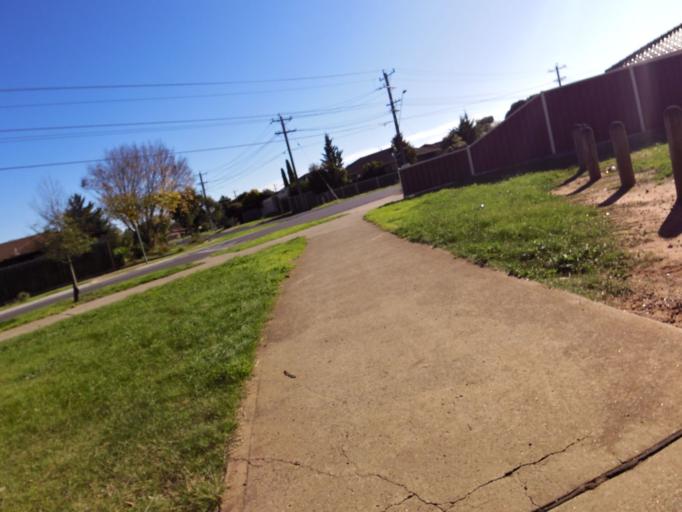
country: AU
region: Victoria
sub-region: Wyndham
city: Tarneit
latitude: -37.8829
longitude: 144.6685
